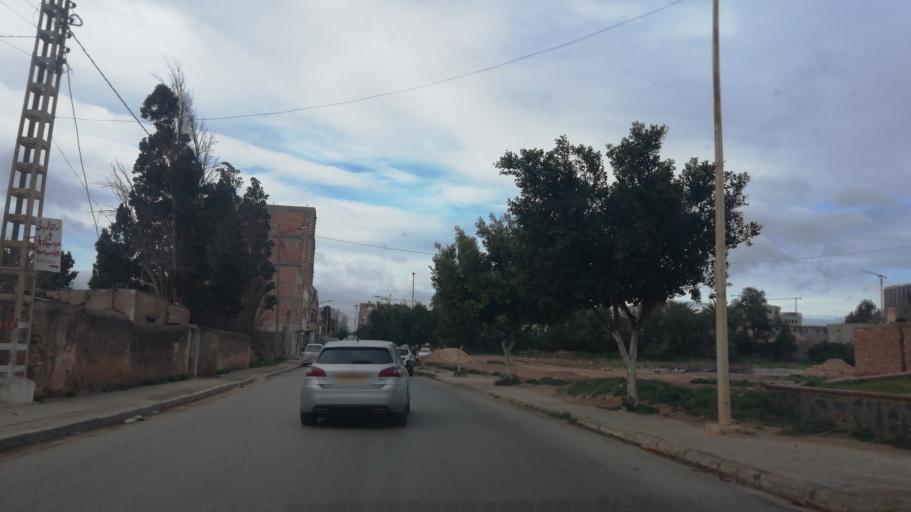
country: DZ
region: Oran
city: Bir el Djir
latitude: 35.7209
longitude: -0.5644
